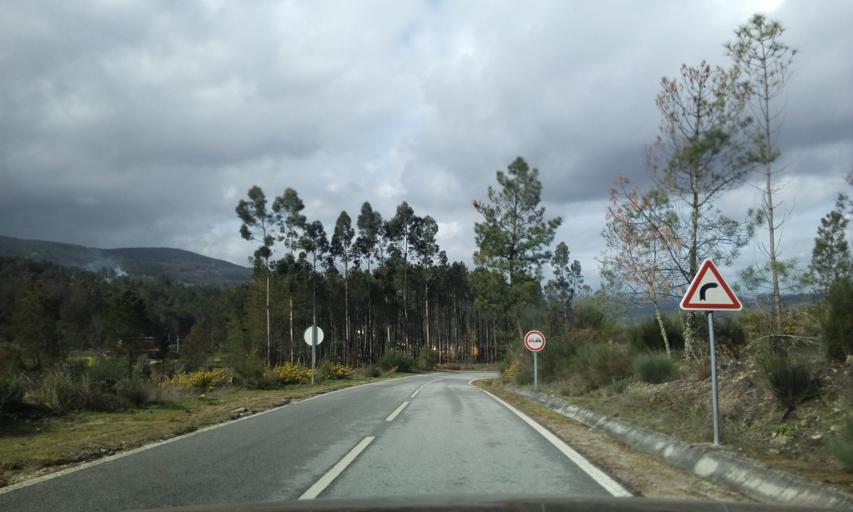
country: PT
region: Guarda
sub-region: Fornos de Algodres
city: Fornos de Algodres
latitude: 40.6620
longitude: -7.6438
